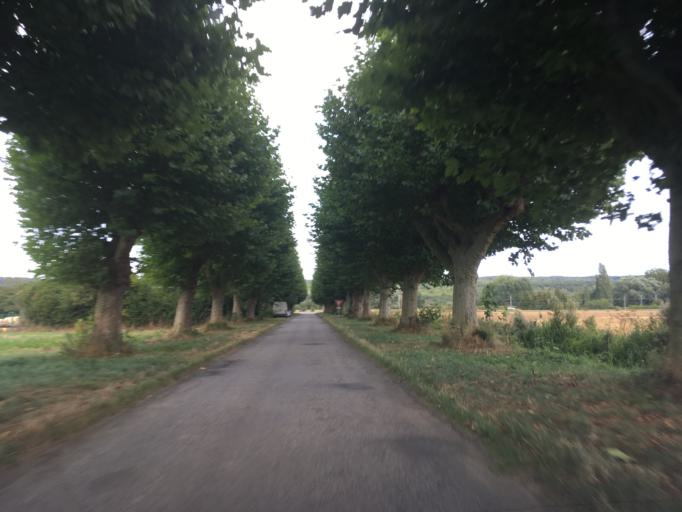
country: FR
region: Haute-Normandie
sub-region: Departement de l'Eure
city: Saint-Just
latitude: 49.1146
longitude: 1.4444
